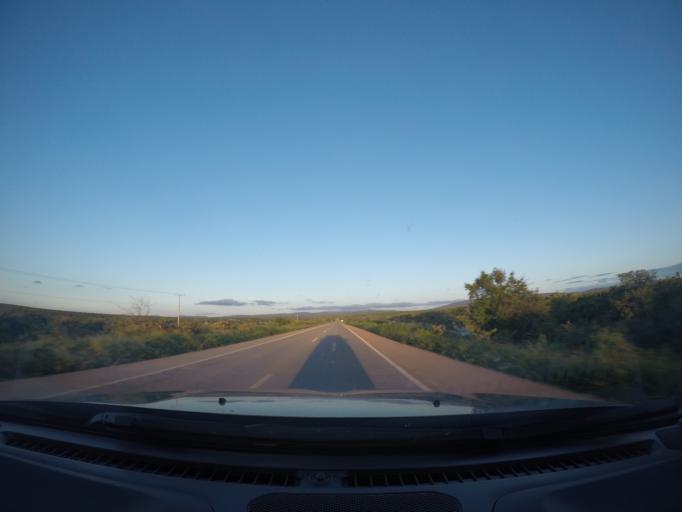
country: BR
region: Bahia
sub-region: Seabra
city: Seabra
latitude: -12.3992
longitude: -41.9404
